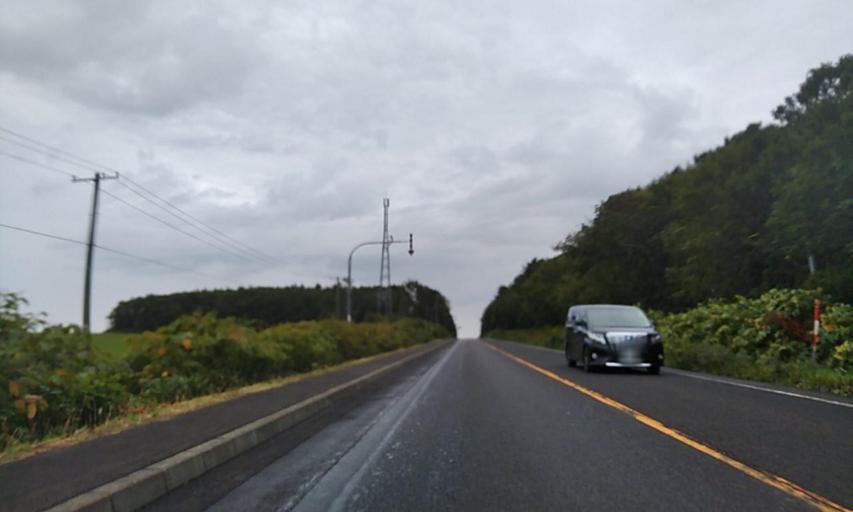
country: JP
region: Hokkaido
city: Mombetsu
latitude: 44.5237
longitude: 143.0510
